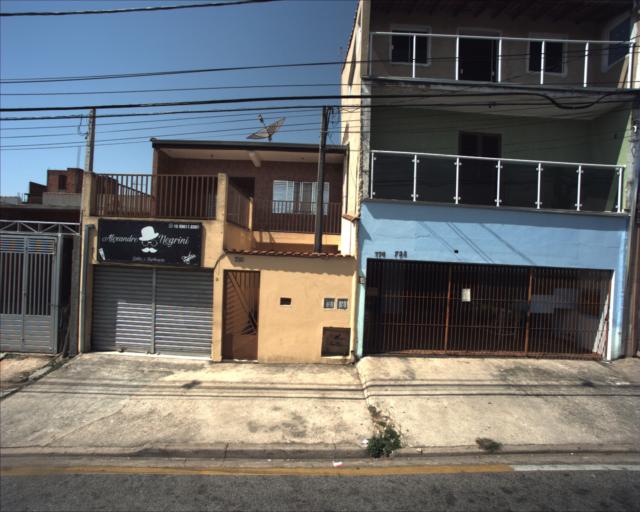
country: BR
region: Sao Paulo
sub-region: Sorocaba
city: Sorocaba
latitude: -23.4490
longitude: -47.4895
